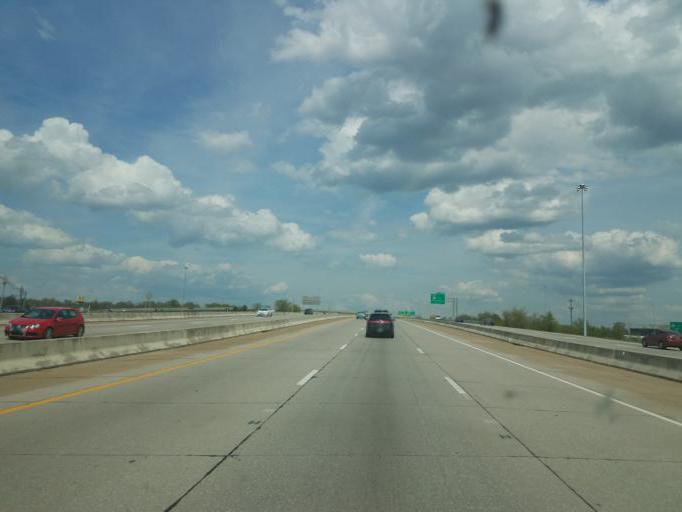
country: US
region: Kentucky
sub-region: Jefferson County
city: Beechwood Village
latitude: 38.2471
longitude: -85.6194
